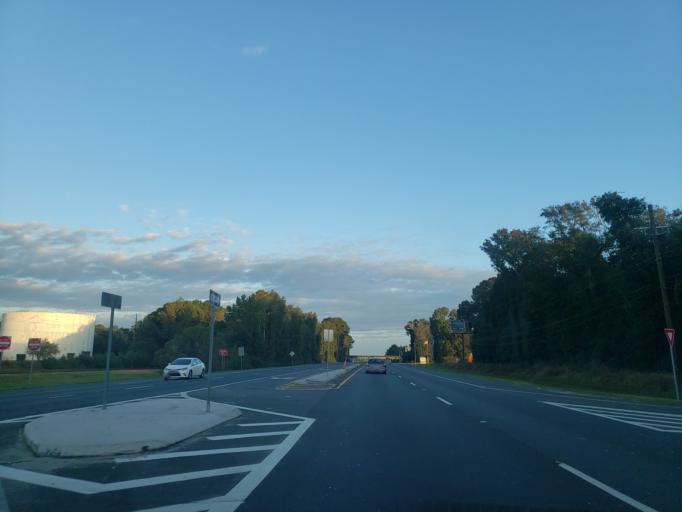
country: US
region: Georgia
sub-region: Chatham County
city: Port Wentworth
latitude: 32.1495
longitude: -81.1790
